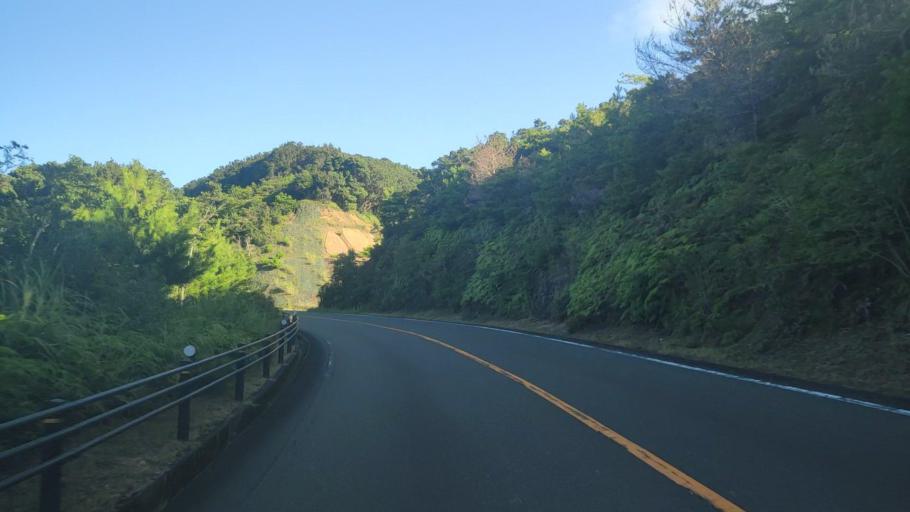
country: JP
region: Mie
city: Toba
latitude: 34.3926
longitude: 136.8610
